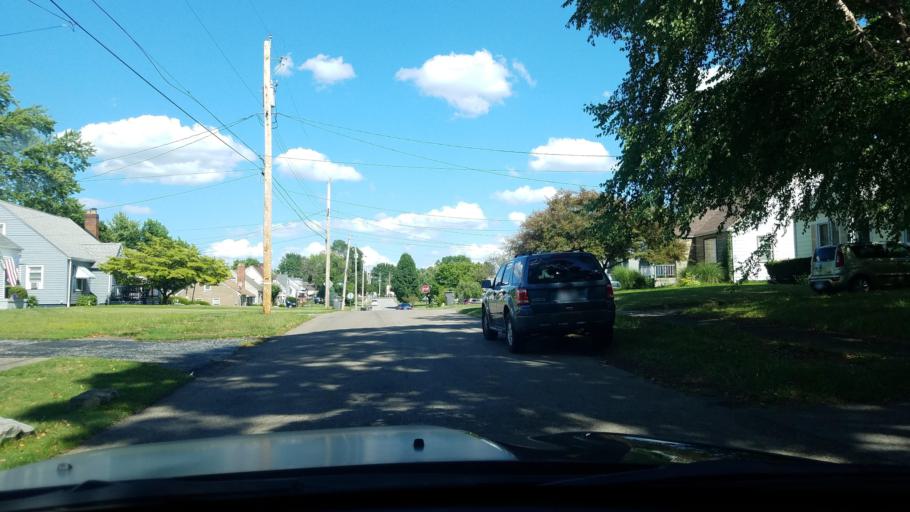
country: US
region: Ohio
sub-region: Mahoning County
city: Struthers
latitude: 41.0577
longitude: -80.6196
